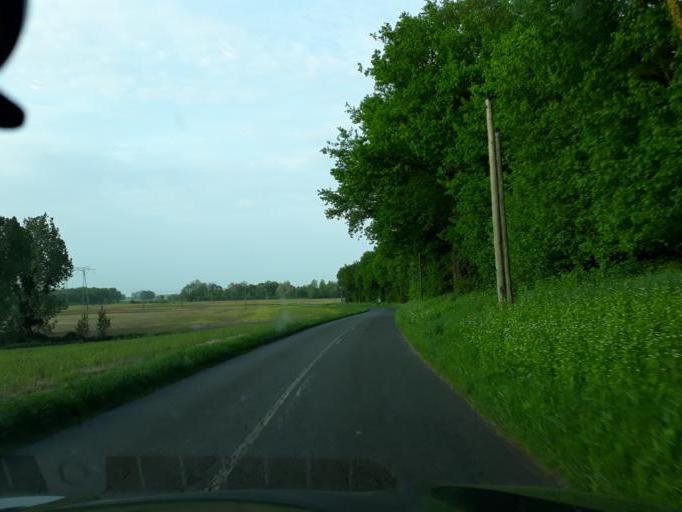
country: FR
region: Centre
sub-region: Departement du Loiret
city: Tavers
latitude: 47.7318
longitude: 1.6377
